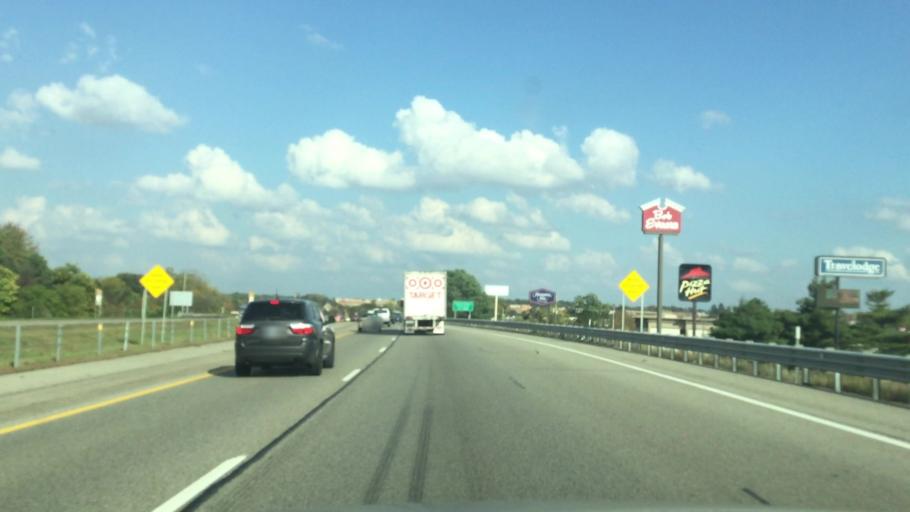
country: US
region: Michigan
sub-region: Calhoun County
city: Lakeview
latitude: 42.2621
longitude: -85.1922
